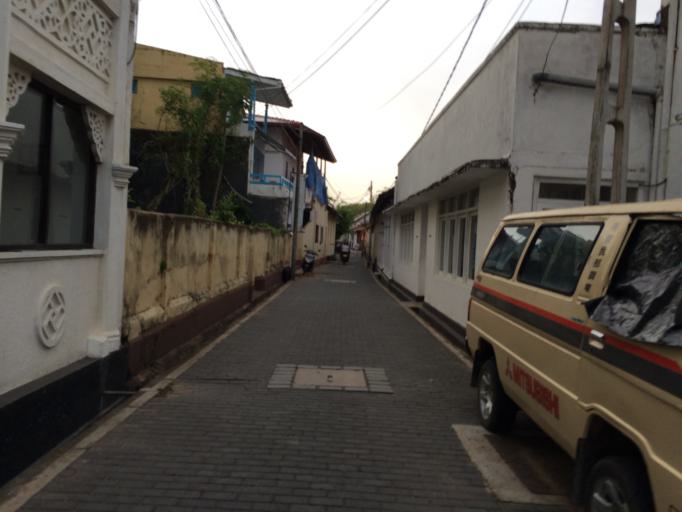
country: LK
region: Southern
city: Galle
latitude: 6.0252
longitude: 80.2172
